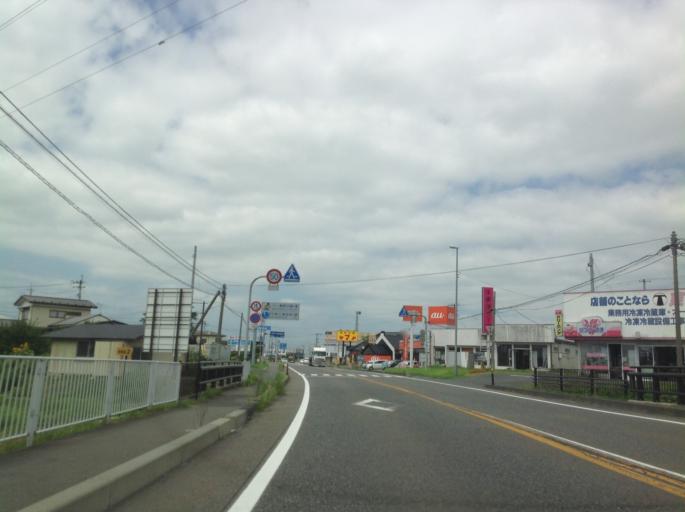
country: JP
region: Iwate
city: Mizusawa
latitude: 39.1544
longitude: 141.1482
